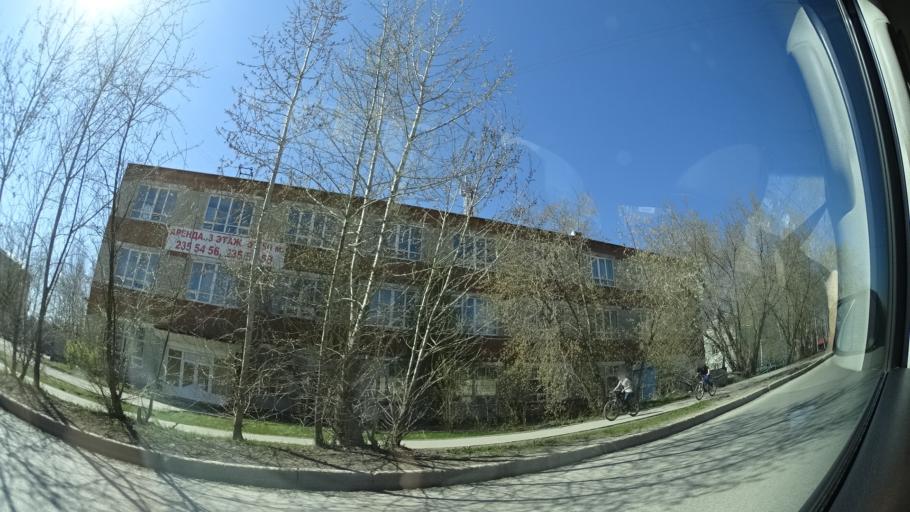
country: RU
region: Perm
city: Perm
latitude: 58.1107
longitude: 56.3040
